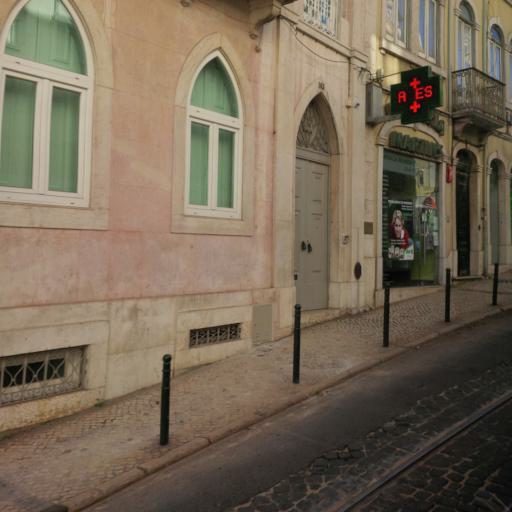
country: PT
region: Lisbon
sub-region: Lisbon
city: Lisbon
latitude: 38.7127
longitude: -9.1579
